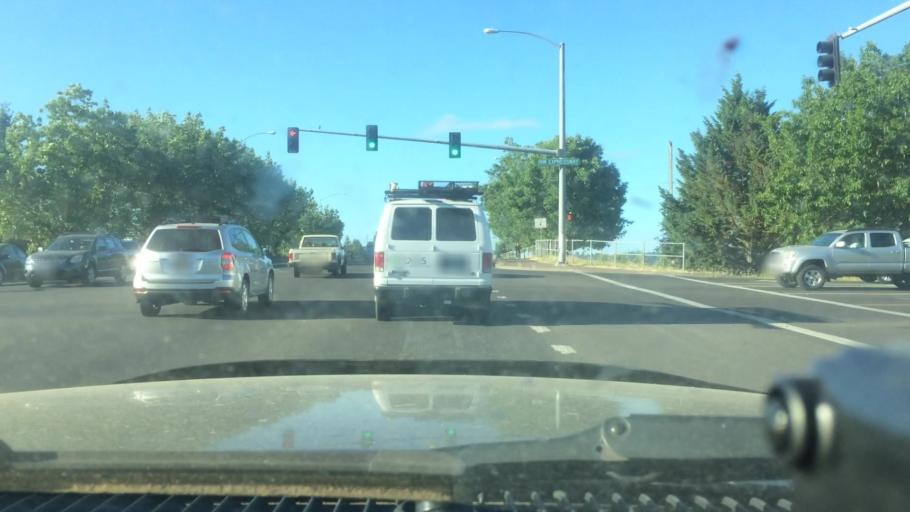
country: US
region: Oregon
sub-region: Lane County
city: Eugene
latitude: 44.0642
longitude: -123.1174
